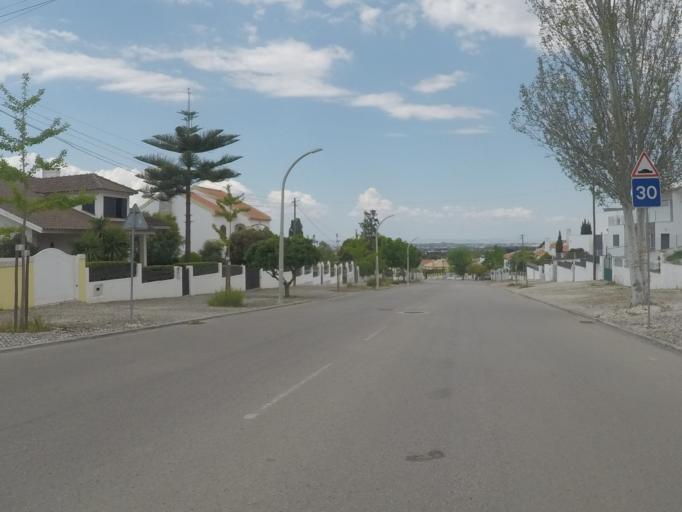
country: PT
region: Setubal
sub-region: Palmela
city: Quinta do Anjo
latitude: 38.5167
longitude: -9.0087
